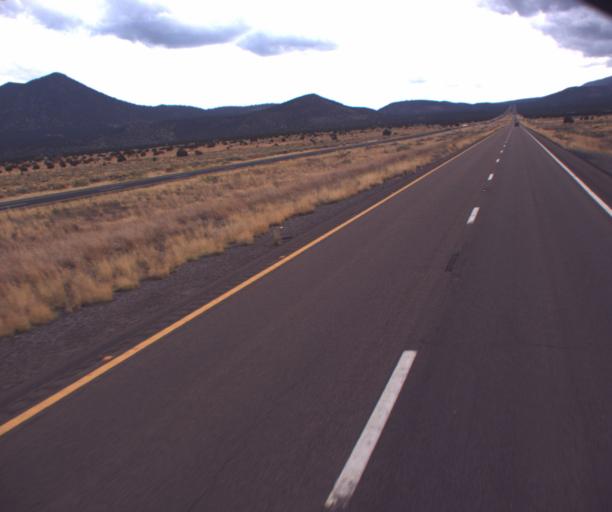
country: US
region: Arizona
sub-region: Coconino County
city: Flagstaff
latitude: 35.4493
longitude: -111.5636
